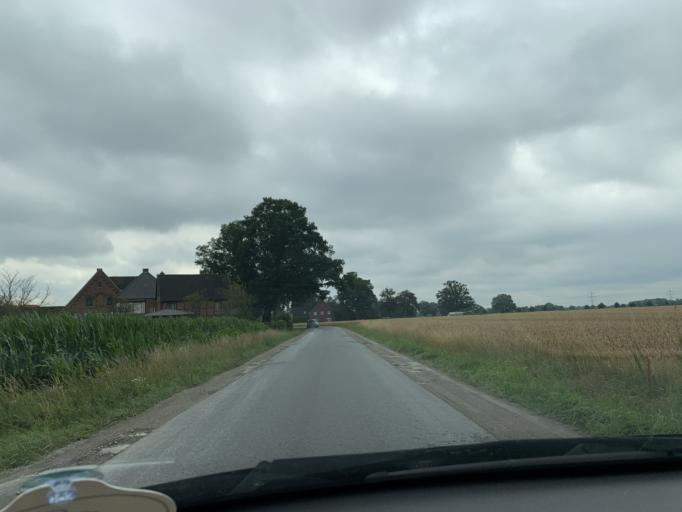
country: DE
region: North Rhine-Westphalia
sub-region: Regierungsbezirk Munster
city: Ennigerloh
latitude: 51.8511
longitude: 8.0825
